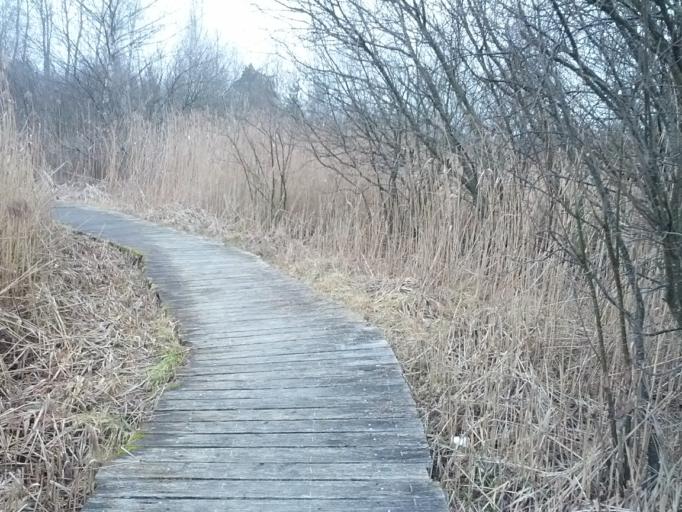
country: DE
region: Baden-Wuerttemberg
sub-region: Tuebingen Region
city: Bad Wurzach
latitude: 47.9072
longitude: 9.8609
